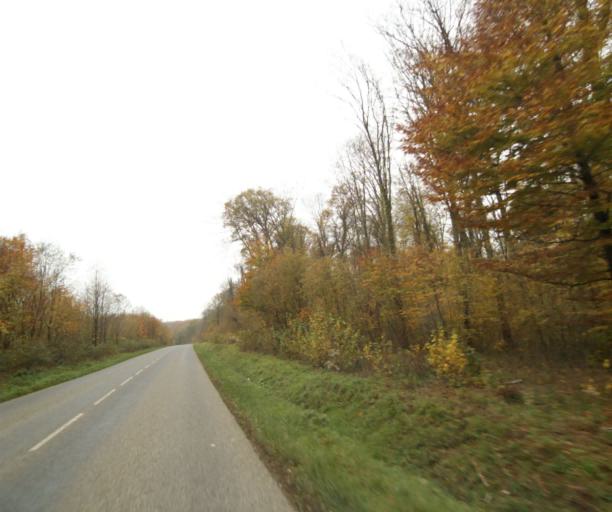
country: FR
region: Lorraine
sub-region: Departement de Meurthe-et-Moselle
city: Joeuf
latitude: 49.2554
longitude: 5.9978
